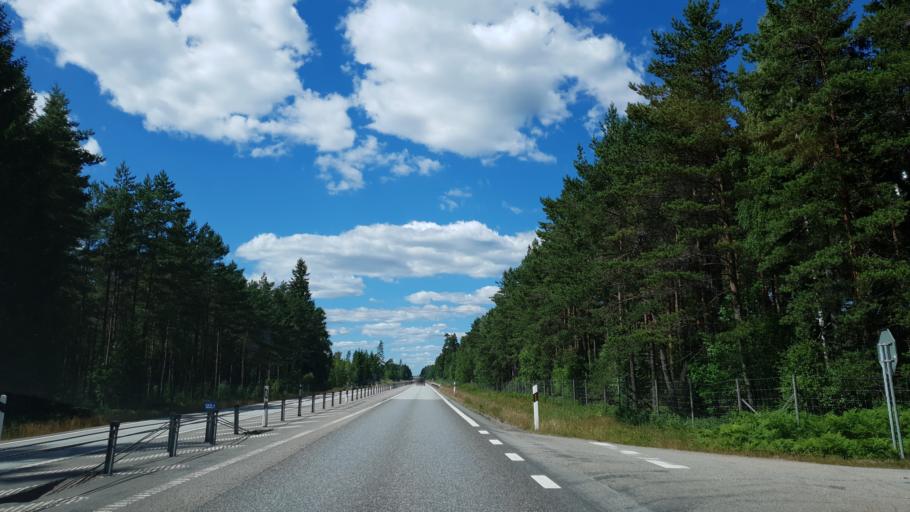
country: SE
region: Kronoberg
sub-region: Lessebo Kommun
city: Hovmantorp
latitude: 56.8289
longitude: 15.0812
